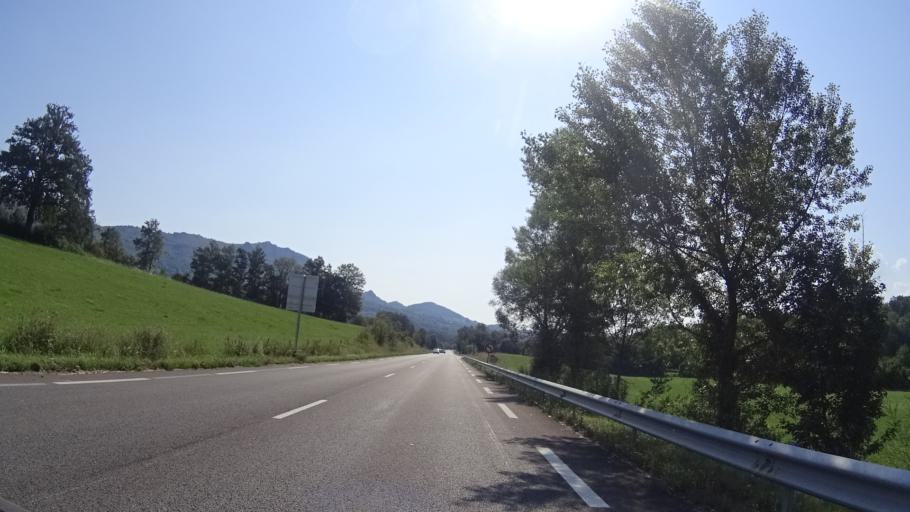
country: FR
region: Midi-Pyrenees
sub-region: Departement de l'Ariege
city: Saint-Paul-de-Jarrat
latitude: 42.9330
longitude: 1.7215
